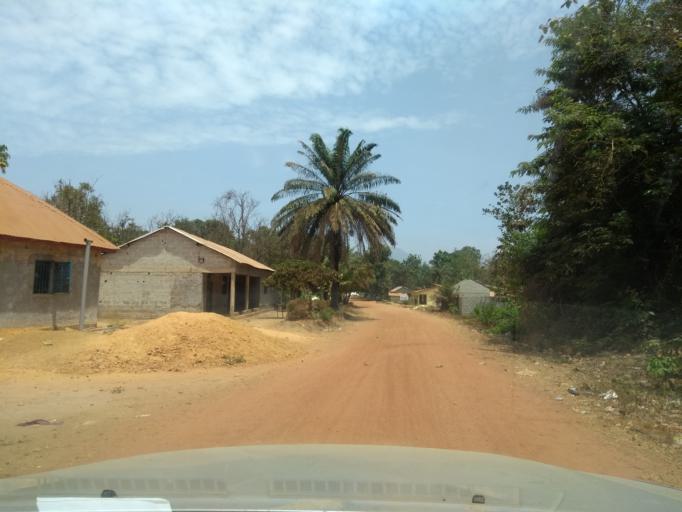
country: GN
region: Kindia
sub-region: Prefecture de Dubreka
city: Dubreka
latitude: 9.7864
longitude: -13.5466
